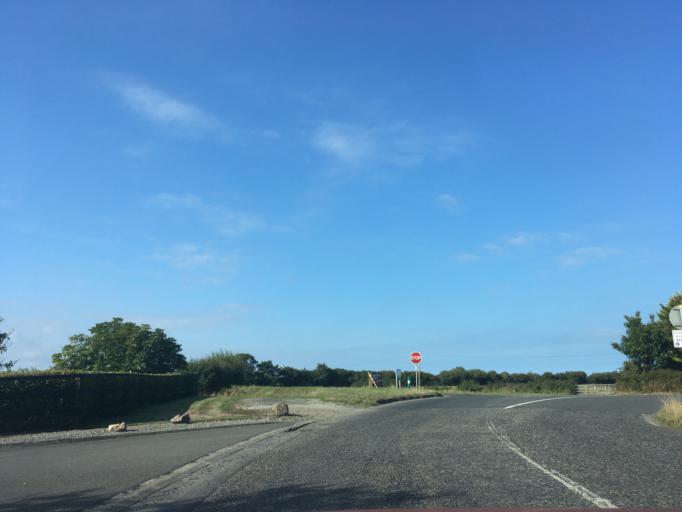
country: IE
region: Leinster
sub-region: Loch Garman
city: Loch Garman
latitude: 52.2834
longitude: -6.4646
